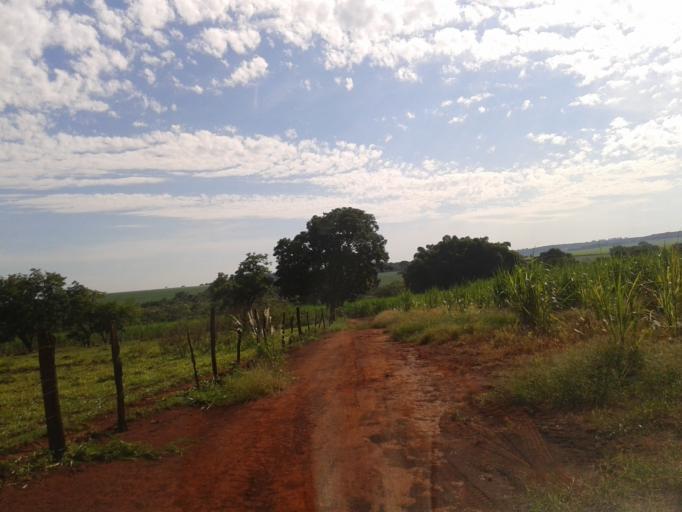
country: BR
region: Minas Gerais
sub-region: Centralina
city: Centralina
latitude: -18.6343
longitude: -49.2485
